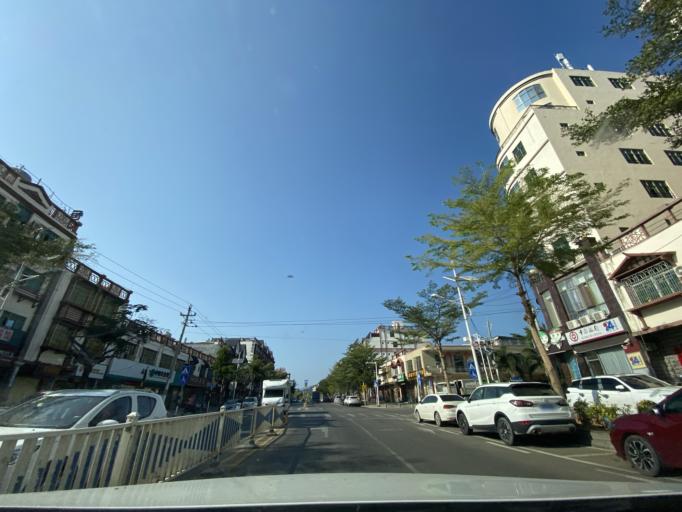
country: CN
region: Hainan
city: Yingzhou
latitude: 18.4277
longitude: 109.8545
